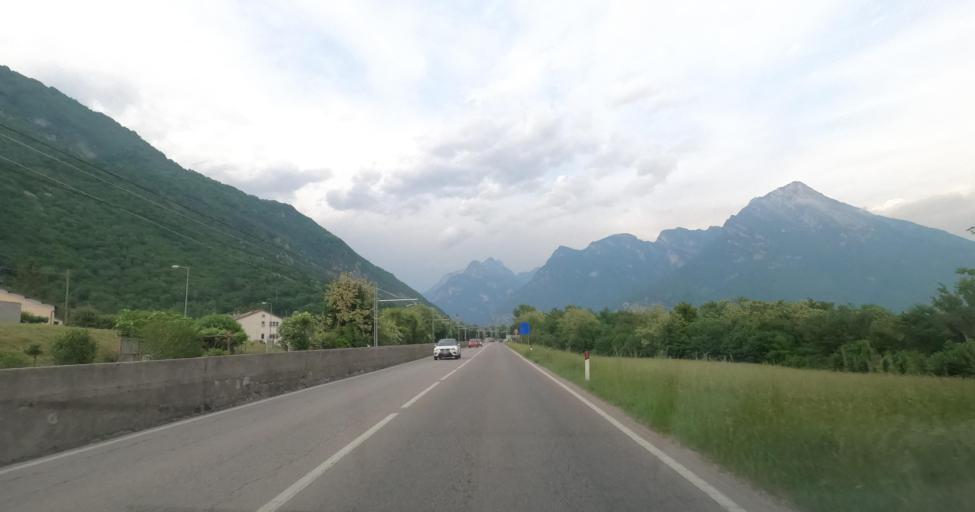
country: IT
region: Veneto
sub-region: Provincia di Belluno
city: Ponte nelle Alpi-Polpet
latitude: 46.1789
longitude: 12.2684
